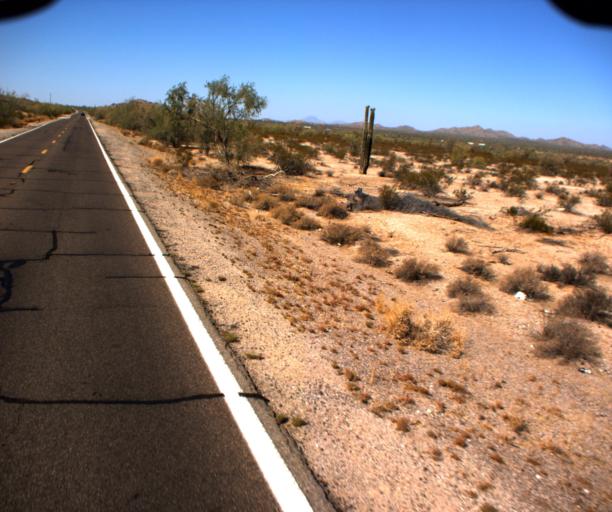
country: US
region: Arizona
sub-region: Pinal County
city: Sacaton
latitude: 33.0215
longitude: -111.7413
